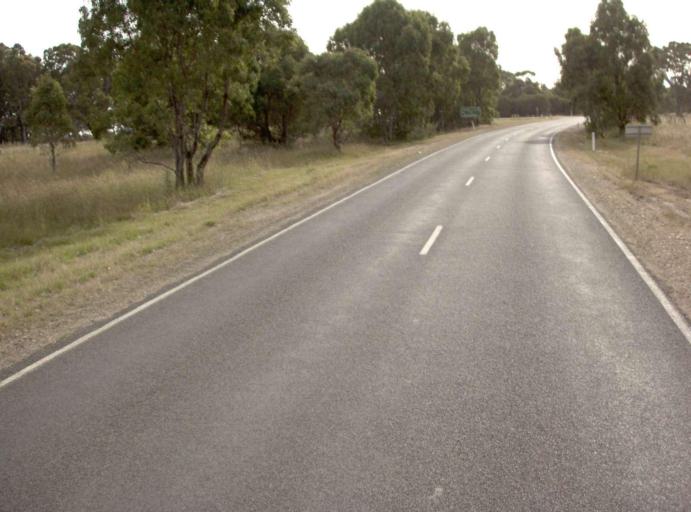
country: AU
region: Victoria
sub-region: Wellington
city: Heyfield
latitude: -38.0602
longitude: 146.6562
